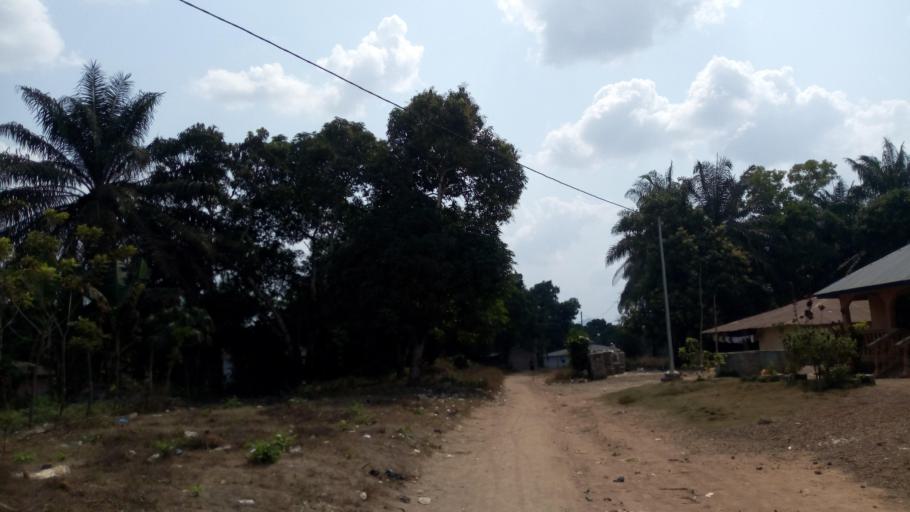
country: SL
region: Southern Province
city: Mogbwemo
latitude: 7.7892
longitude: -12.3017
